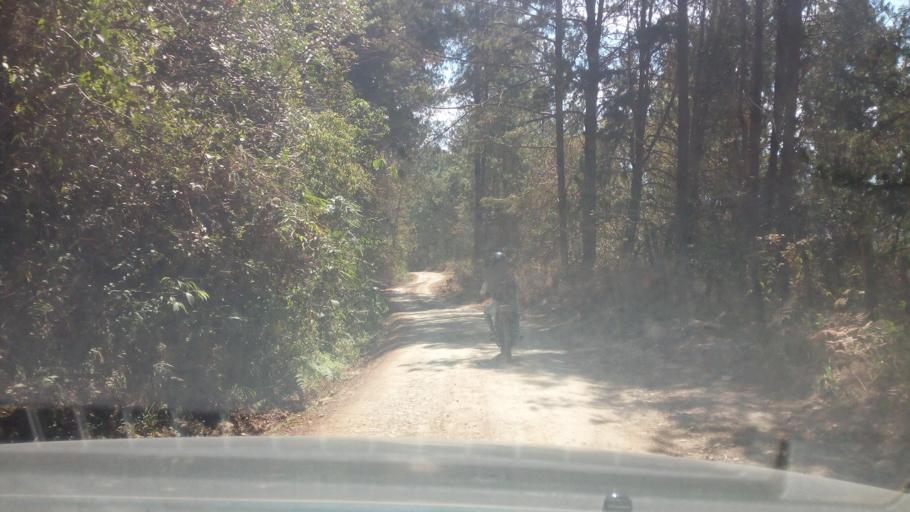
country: CO
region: Boyaca
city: Somondoco
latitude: 4.9926
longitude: -73.4163
